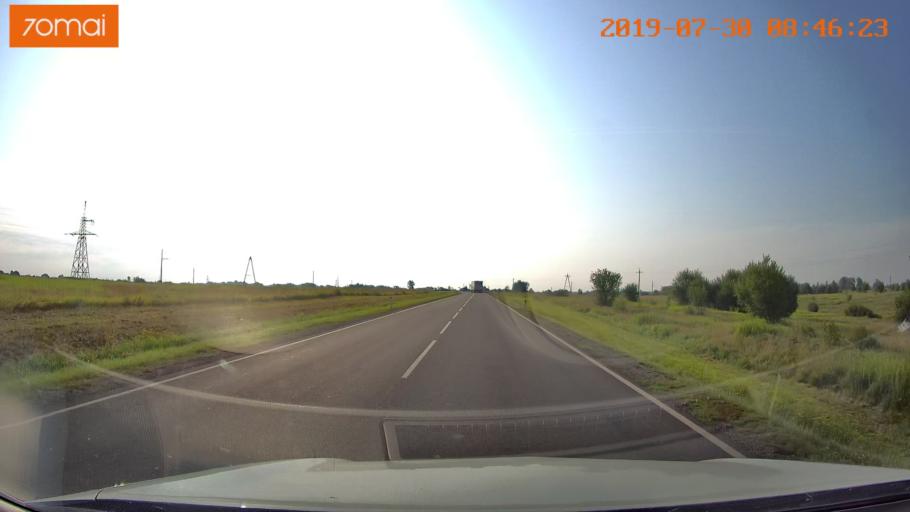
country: RU
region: Kaliningrad
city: Chernyakhovsk
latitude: 54.6236
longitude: 21.8834
